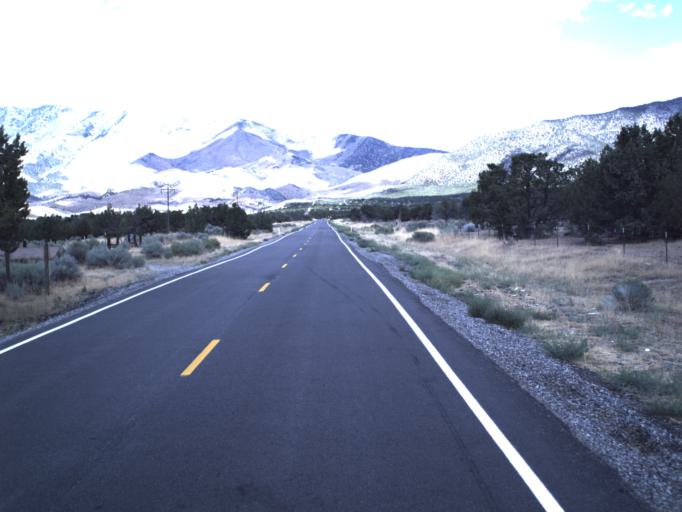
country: US
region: Utah
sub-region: Tooele County
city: Grantsville
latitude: 40.3124
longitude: -112.6359
